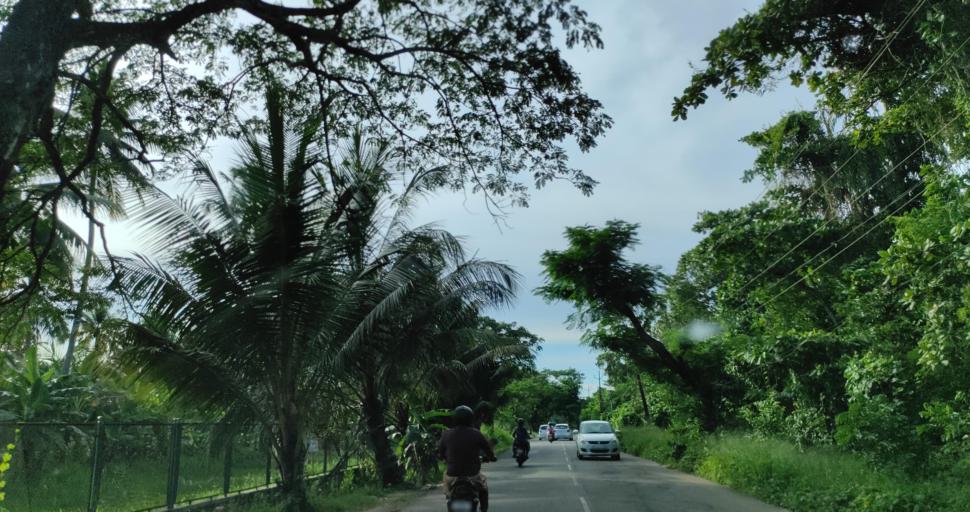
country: IN
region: Kerala
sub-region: Alappuzha
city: Shertallai
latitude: 9.6229
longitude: 76.4299
